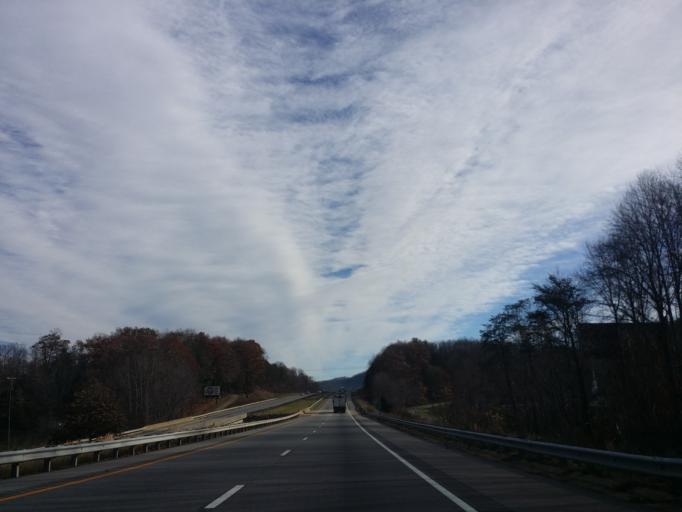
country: US
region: North Carolina
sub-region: Buncombe County
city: Swannanoa
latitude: 35.5992
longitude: -82.3679
